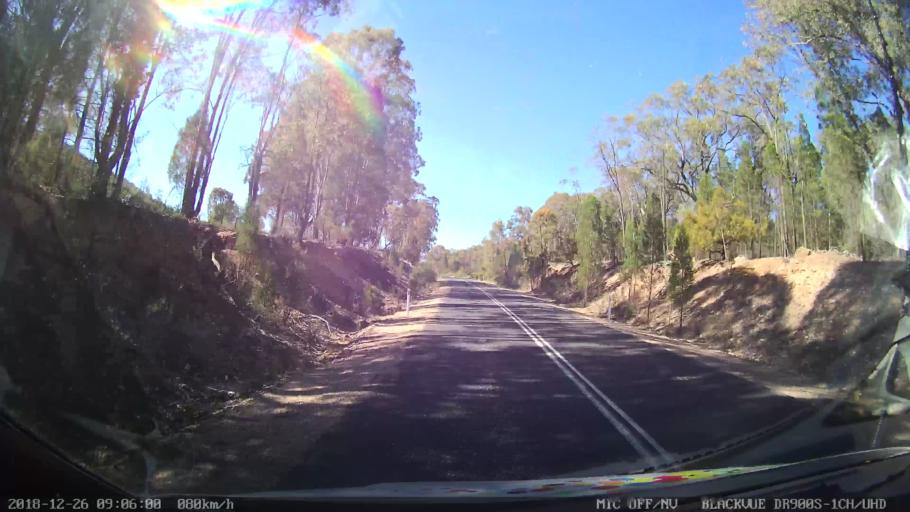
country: AU
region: New South Wales
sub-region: Mid-Western Regional
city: Kandos
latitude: -32.6889
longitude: 150.0046
